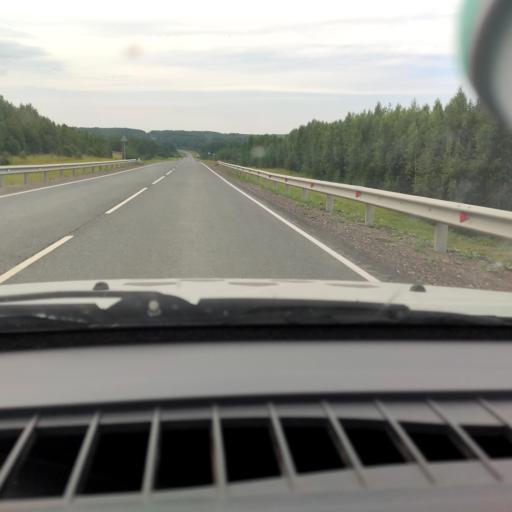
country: RU
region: Kirov
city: Kostino
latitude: 58.8081
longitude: 53.5959
